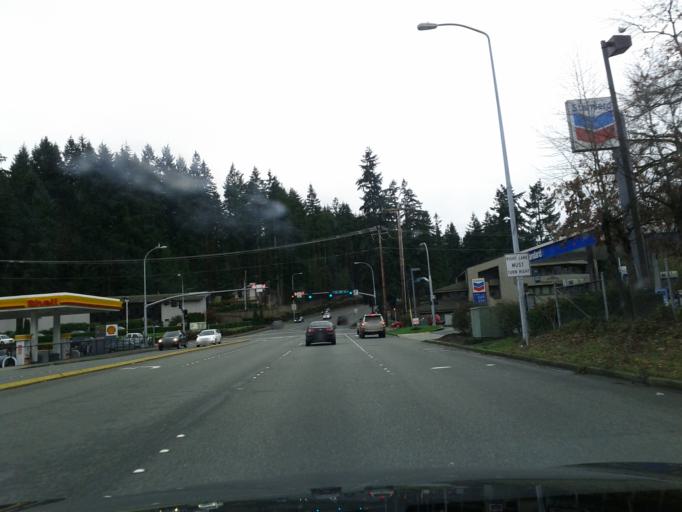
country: US
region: Washington
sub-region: King County
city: Eastgate
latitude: 47.5768
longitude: -122.1403
